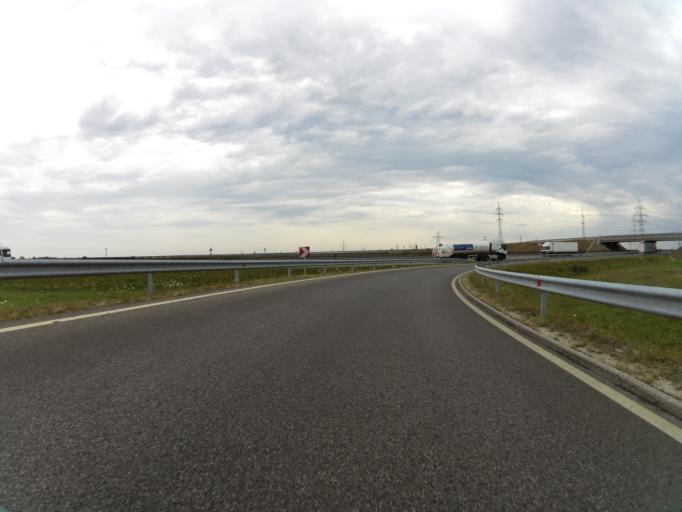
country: HU
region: Csongrad
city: Szeged
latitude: 46.2956
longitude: 20.1363
